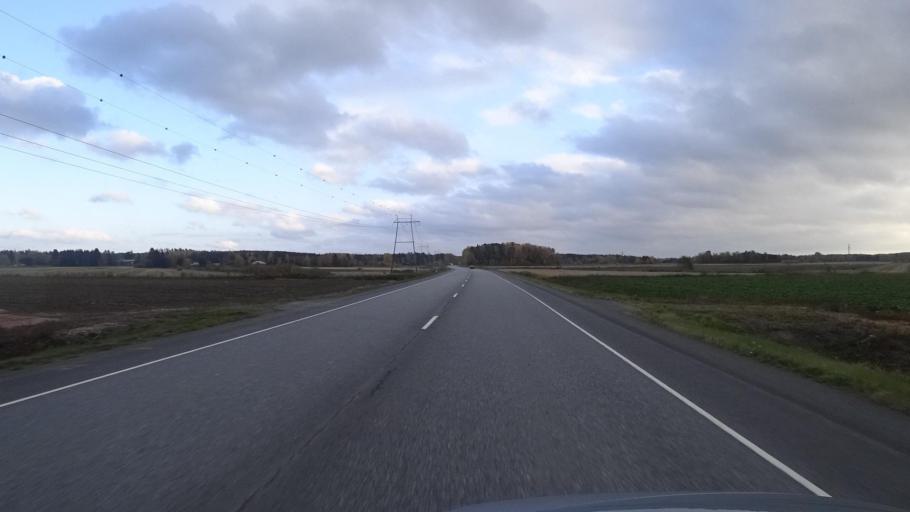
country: FI
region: Satakunta
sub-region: Rauma
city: Saekylae
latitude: 61.0300
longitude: 22.3956
